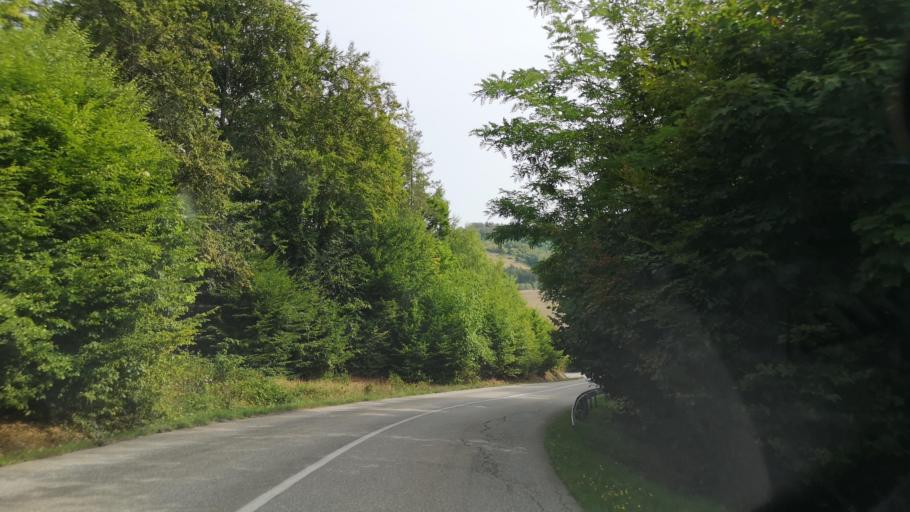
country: SK
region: Banskobystricky
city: Revuca
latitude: 48.5809
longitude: 20.0459
